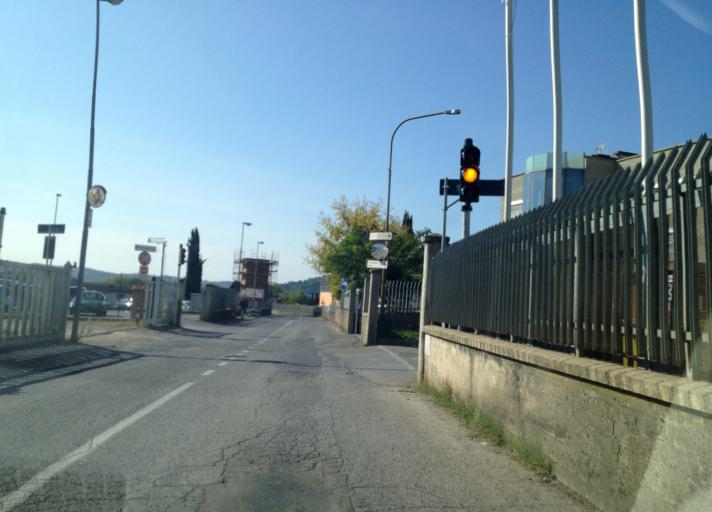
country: IT
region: Tuscany
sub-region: Provincia di Siena
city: Poggibonsi
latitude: 43.4814
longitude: 11.1345
